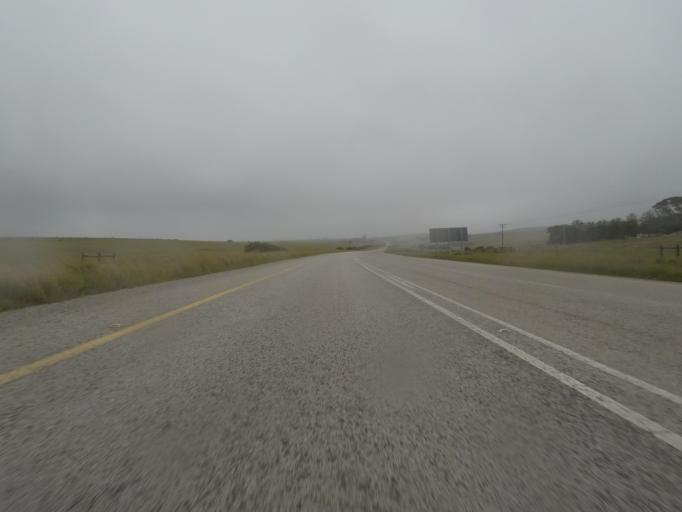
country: ZA
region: Eastern Cape
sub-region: Cacadu District Municipality
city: Grahamstown
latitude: -33.6279
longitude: 26.3099
